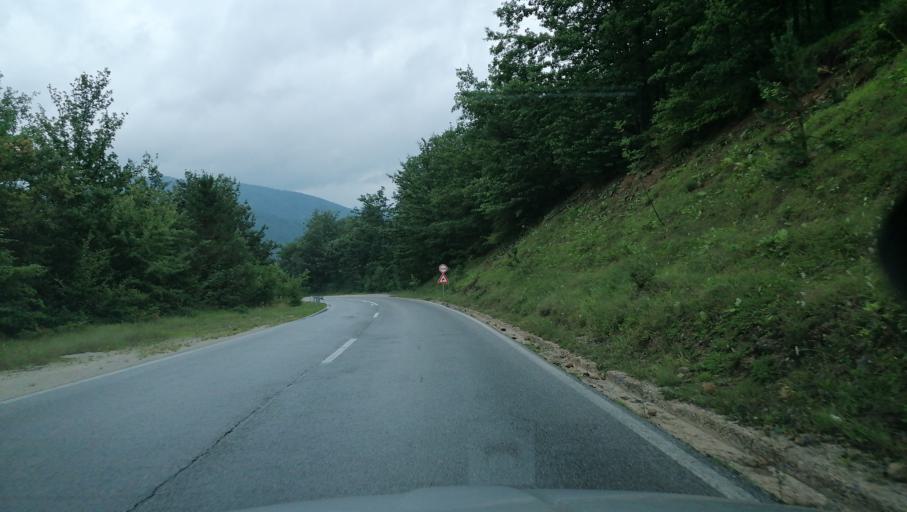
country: RS
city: Durici
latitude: 43.8064
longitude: 19.5106
